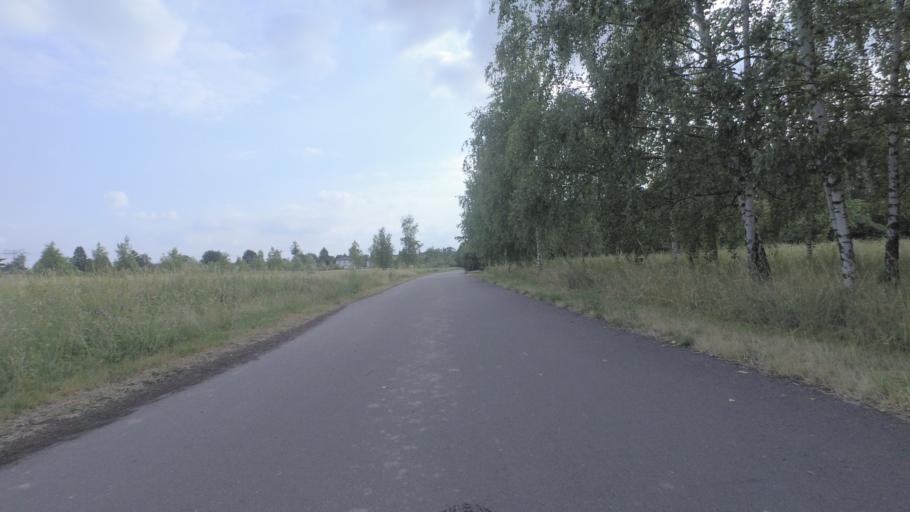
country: DE
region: Berlin
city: Altglienicke
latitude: 52.4033
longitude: 13.5183
